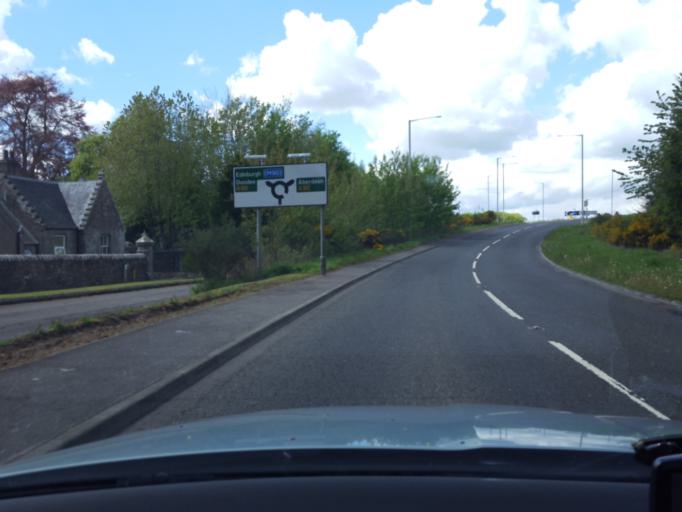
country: GB
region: Scotland
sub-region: Angus
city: Brechin
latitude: 56.7281
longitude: -2.6950
